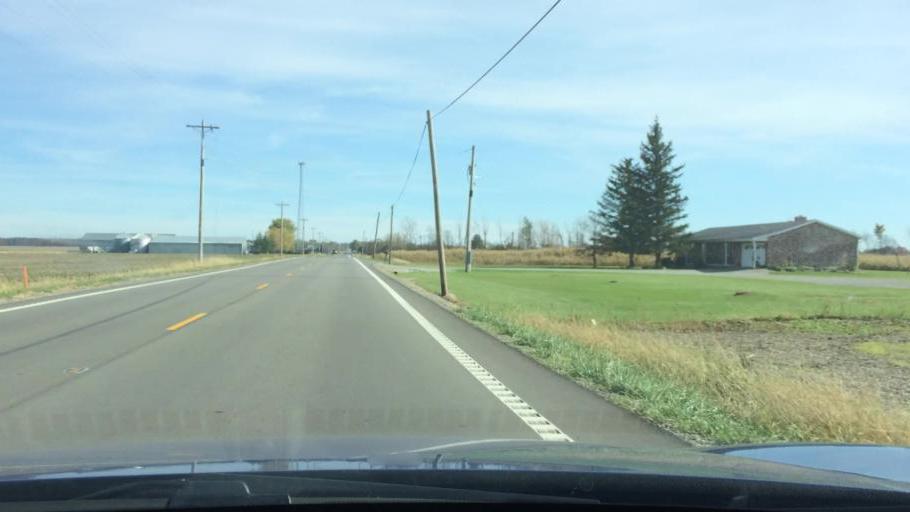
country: US
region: Ohio
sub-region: Logan County
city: Russells Point
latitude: 40.4394
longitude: -83.8984
